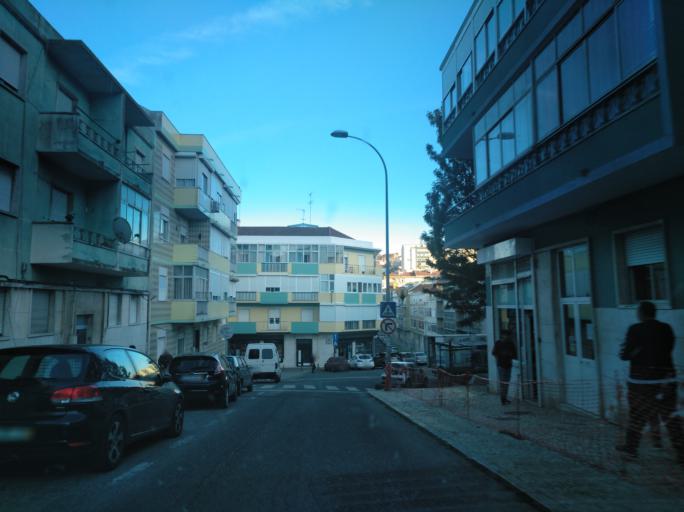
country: PT
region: Lisbon
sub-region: Amadora
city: Amadora
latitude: 38.7472
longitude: -9.2189
